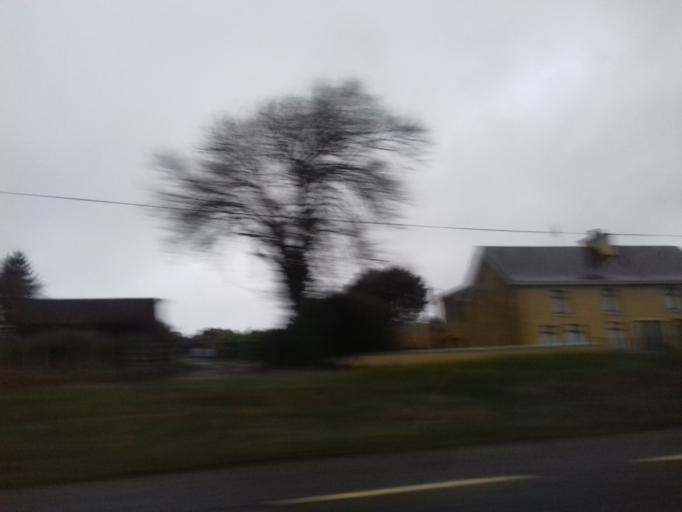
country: IE
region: Munster
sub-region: Ciarrai
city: Castleisland
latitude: 52.2854
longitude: -9.4063
